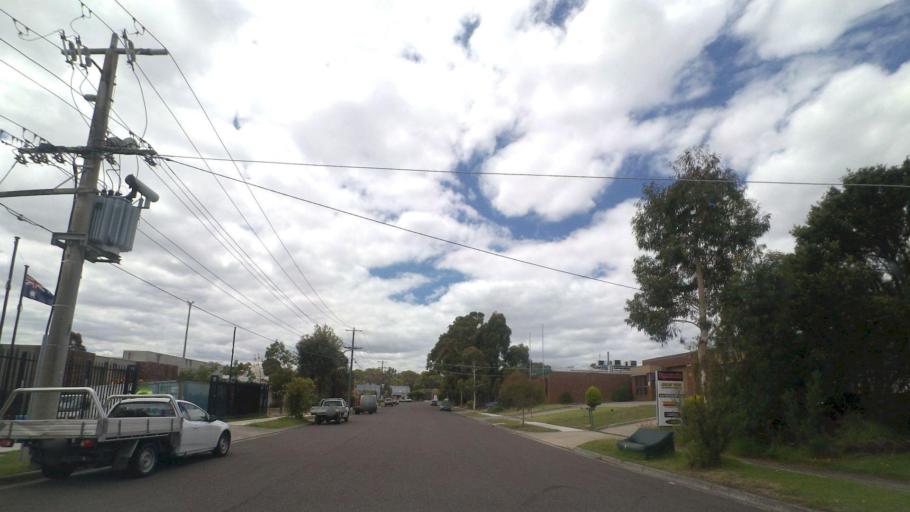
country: AU
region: Victoria
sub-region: Knox
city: Bayswater
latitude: -37.8675
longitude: 145.2539
